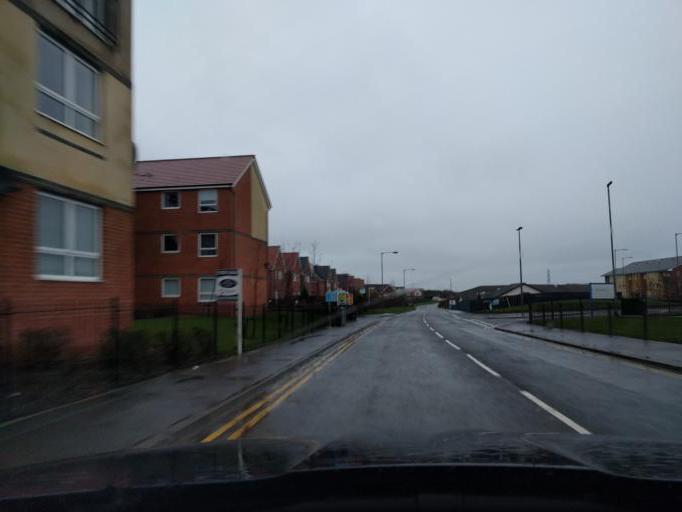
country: GB
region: England
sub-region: Northumberland
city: Lynemouth
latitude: 55.1853
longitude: -1.5476
